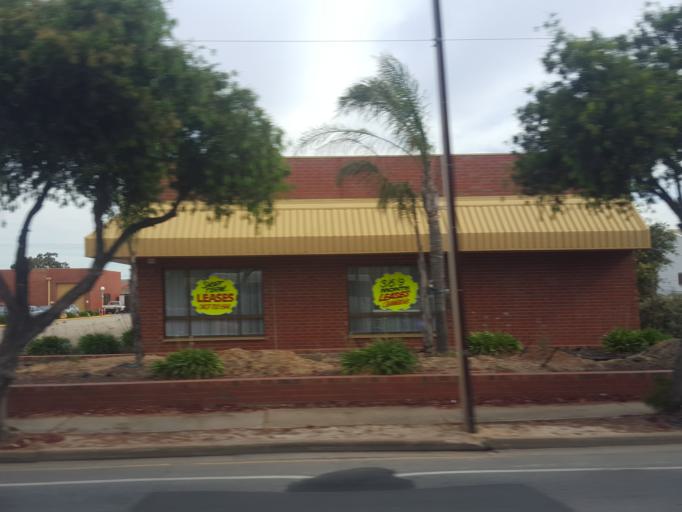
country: AU
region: South Australia
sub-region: Charles Sturt
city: Woodville North
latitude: -34.8506
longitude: 138.5454
